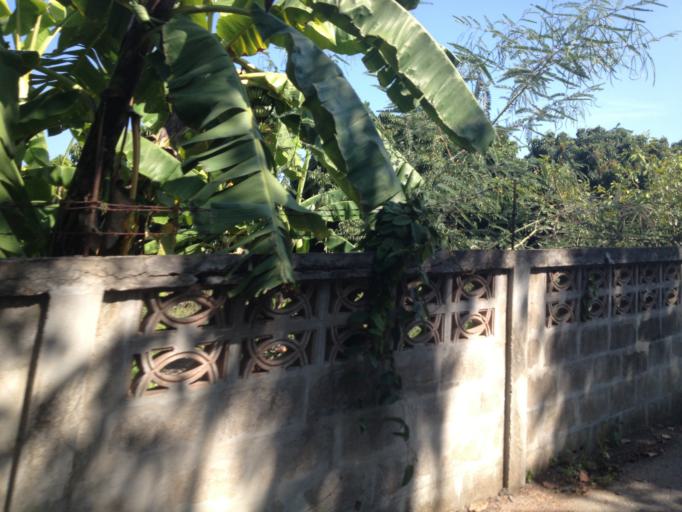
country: TH
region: Chiang Mai
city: Hang Dong
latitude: 18.6934
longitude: 98.9279
